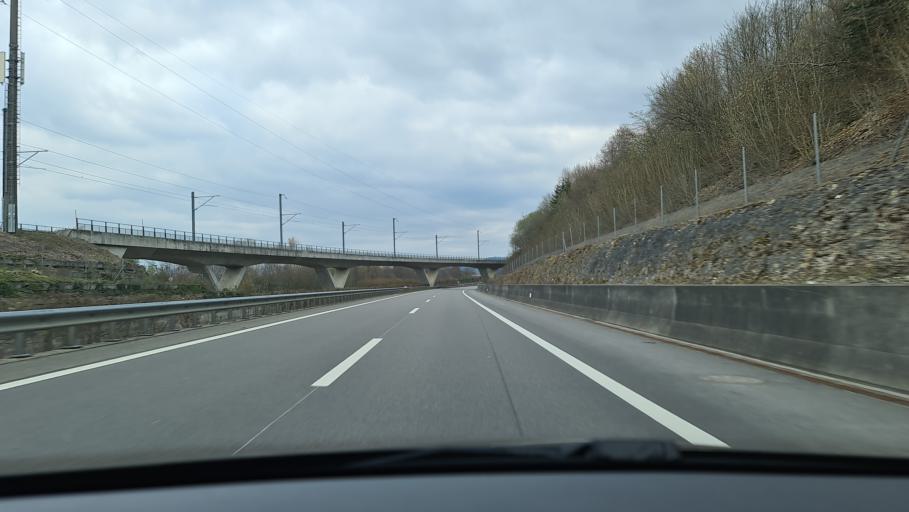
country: CH
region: Jura
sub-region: Porrentruy District
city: Alle
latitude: 47.4177
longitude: 7.1186
